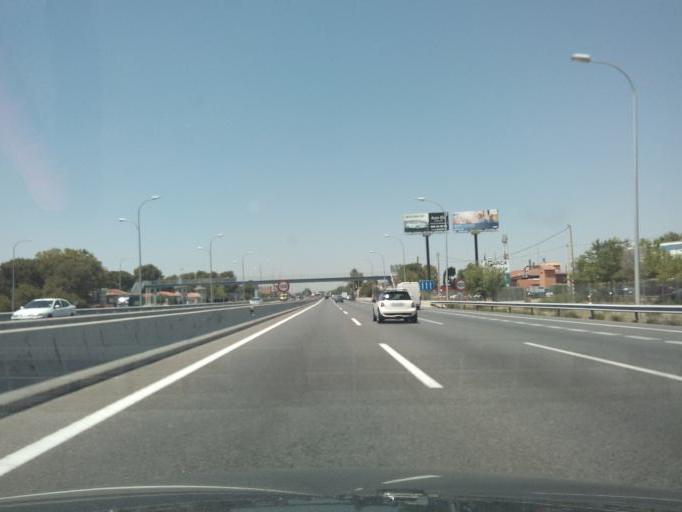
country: ES
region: Madrid
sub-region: Provincia de Madrid
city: San Fernando de Henares
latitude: 40.4484
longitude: -3.5469
